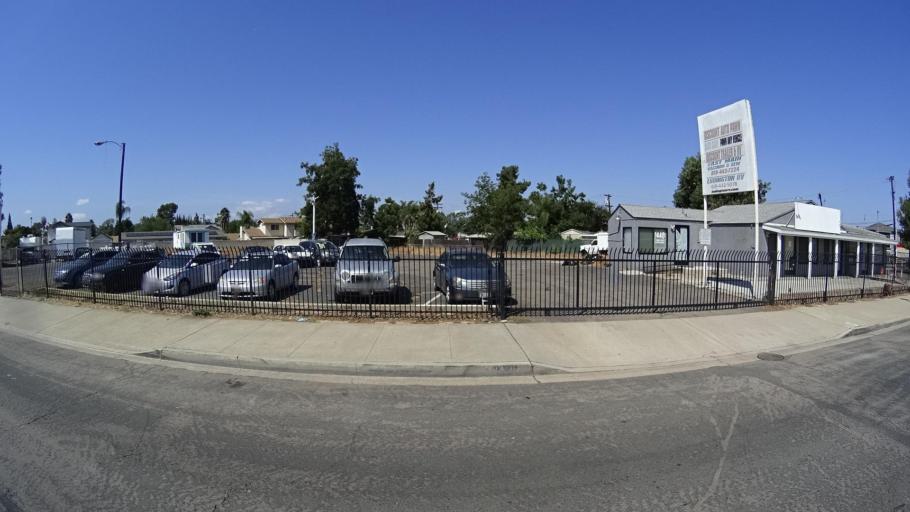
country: US
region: California
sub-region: San Diego County
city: Bostonia
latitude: 32.8014
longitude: -116.9293
